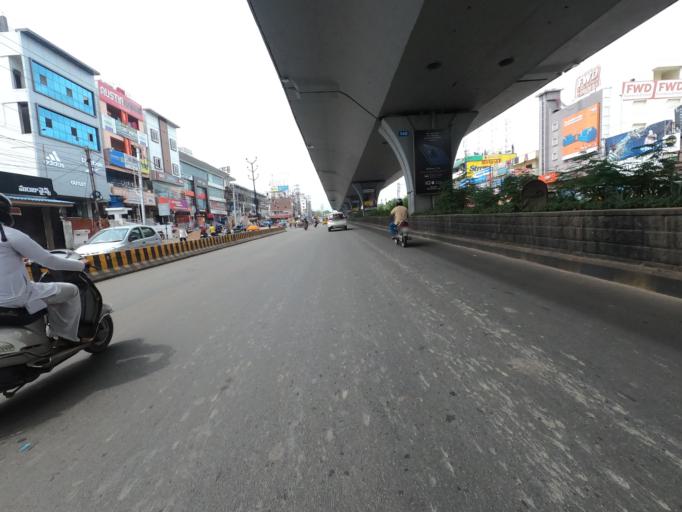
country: IN
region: Telangana
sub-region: Hyderabad
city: Hyderabad
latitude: 17.3651
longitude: 78.4285
